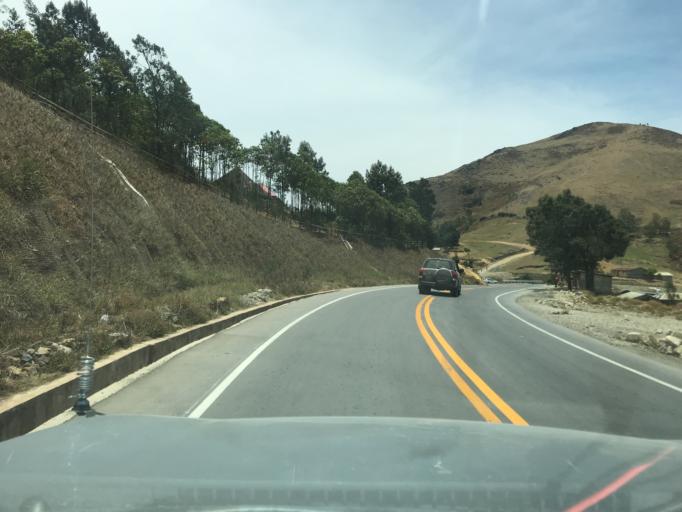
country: TL
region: Manufahi
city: Same
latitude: -8.8783
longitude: 125.6031
